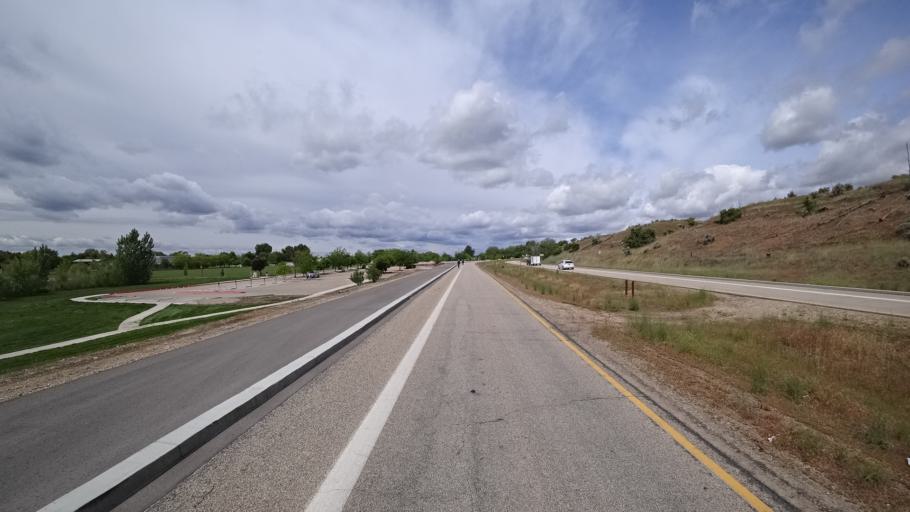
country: US
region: Idaho
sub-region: Ada County
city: Eagle
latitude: 43.6913
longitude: -116.3092
